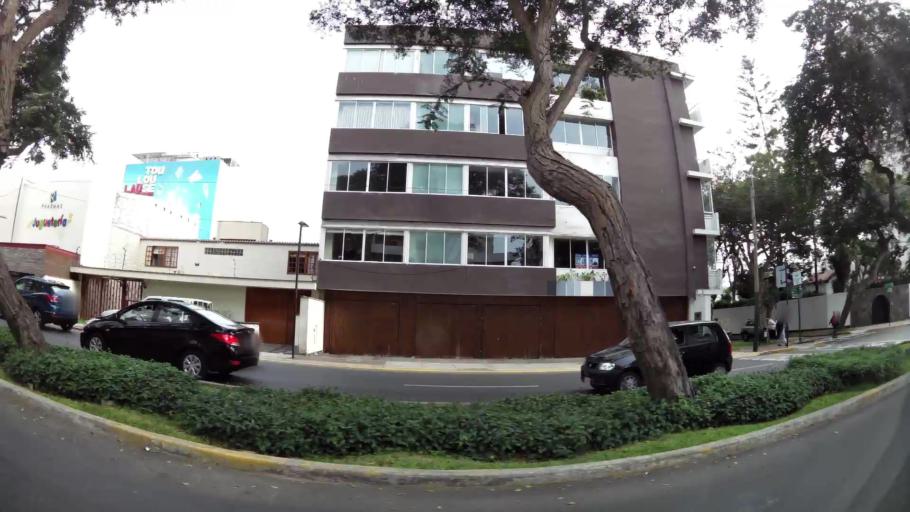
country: PE
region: Lima
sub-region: Lima
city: San Isidro
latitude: -12.0975
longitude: -77.0566
